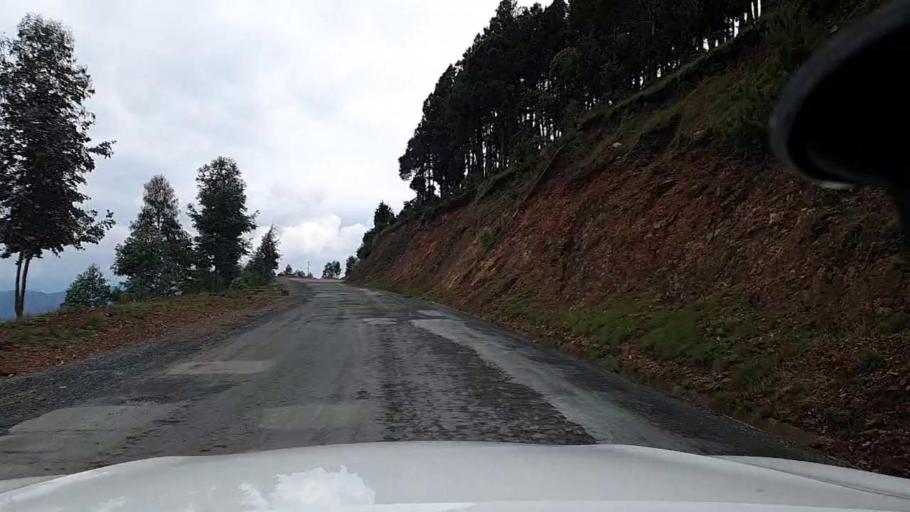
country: RW
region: Southern Province
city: Gitarama
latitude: -2.0668
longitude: 29.5619
